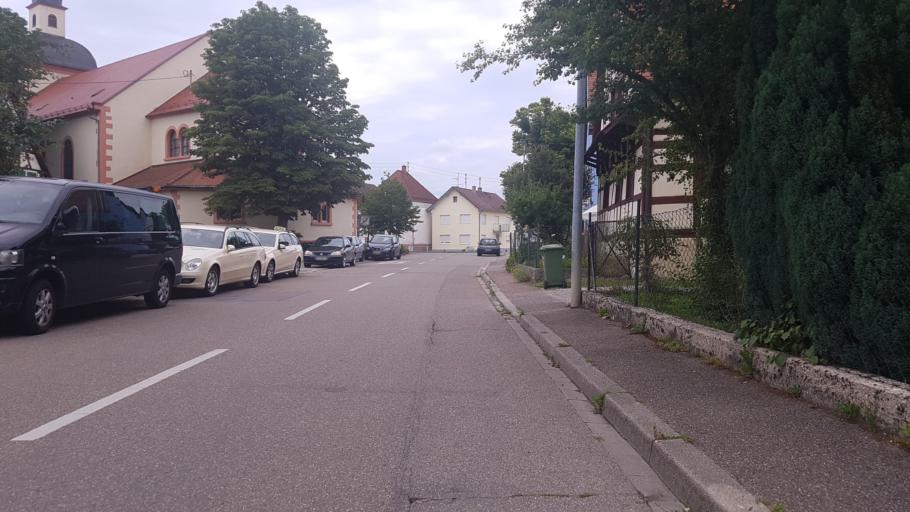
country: DE
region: Baden-Wuerttemberg
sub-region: Karlsruhe Region
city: Rheinau
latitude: 48.8608
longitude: 8.1552
